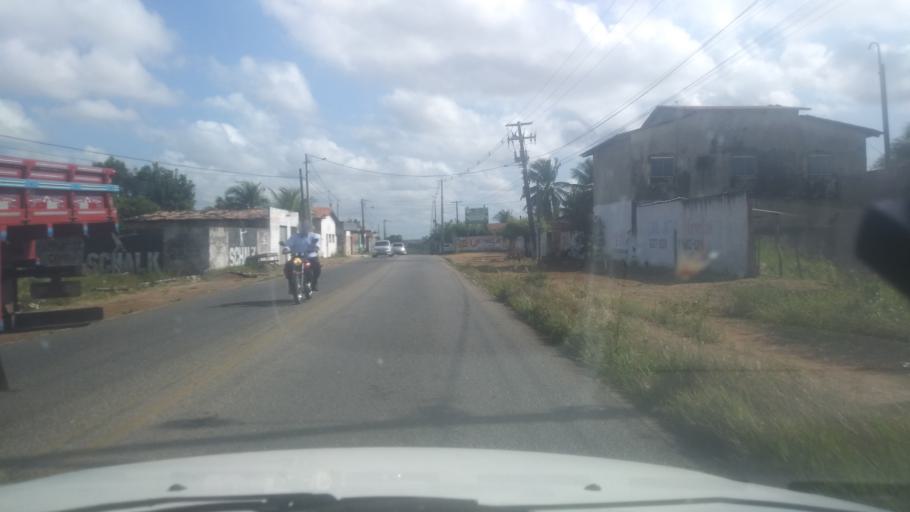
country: BR
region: Rio Grande do Norte
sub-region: Extremoz
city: Extremoz
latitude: -5.7142
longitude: -35.2775
